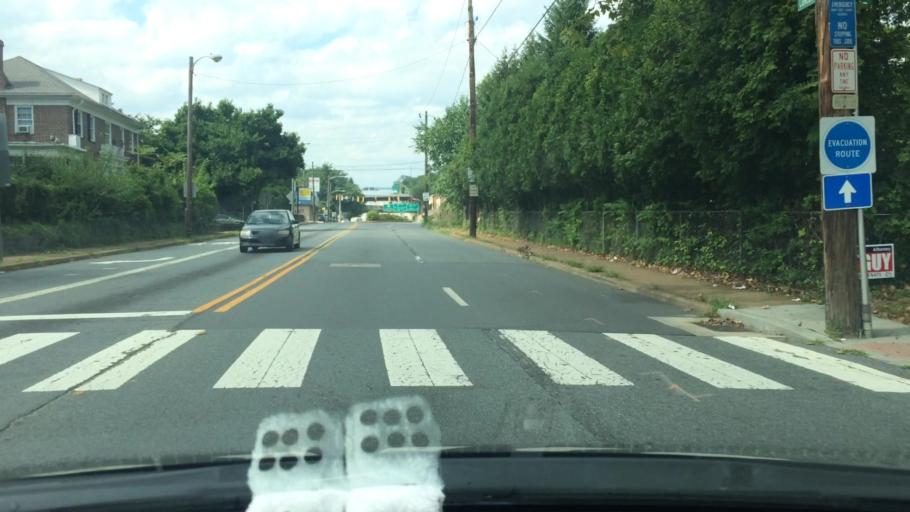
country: US
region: Delaware
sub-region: New Castle County
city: Wilmington
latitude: 39.7616
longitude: -75.5423
